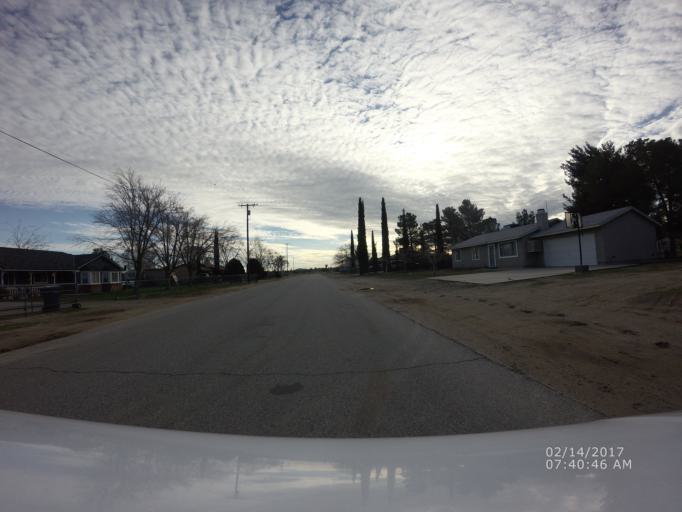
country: US
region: California
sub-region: Los Angeles County
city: Littlerock
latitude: 34.5483
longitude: -117.9419
